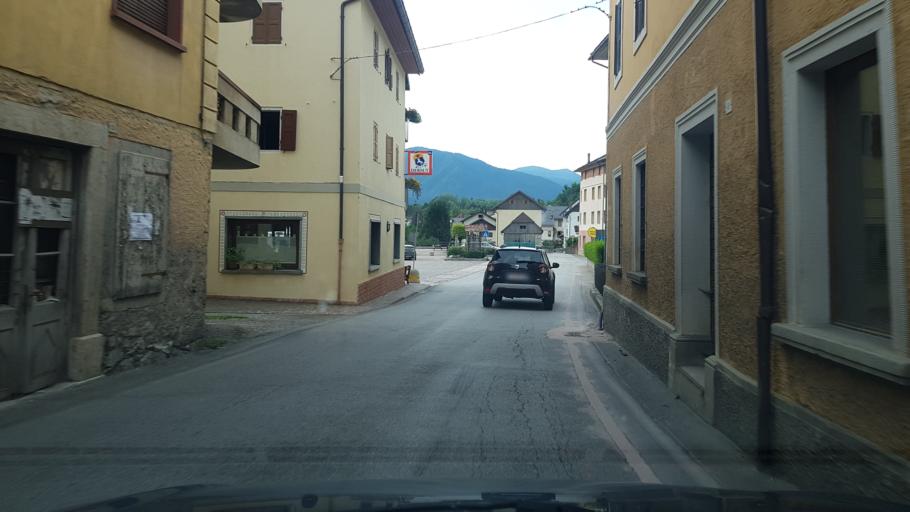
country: IT
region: Friuli Venezia Giulia
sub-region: Provincia di Udine
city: Rigolato
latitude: 46.5530
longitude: 12.8512
